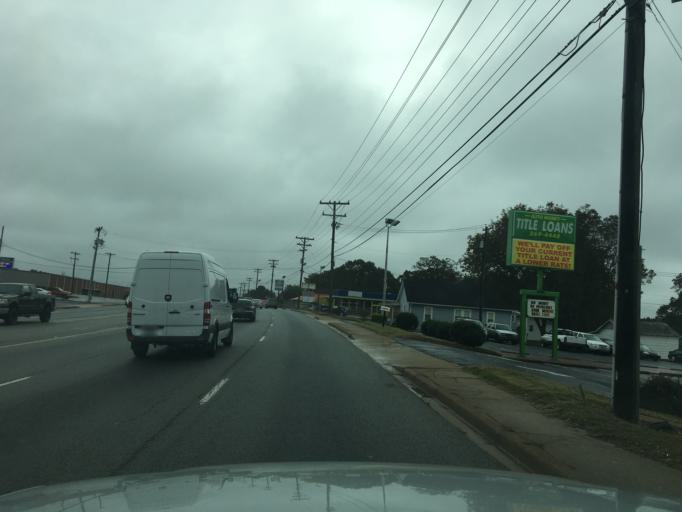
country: US
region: South Carolina
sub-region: Greenville County
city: Welcome
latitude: 34.8126
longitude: -82.4401
